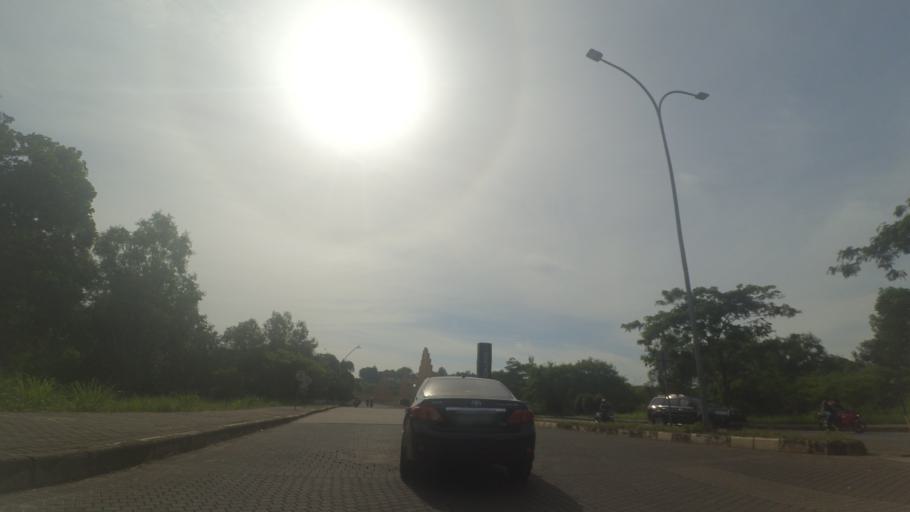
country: ID
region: West Java
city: Pamulang
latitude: -6.3461
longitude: 106.7725
